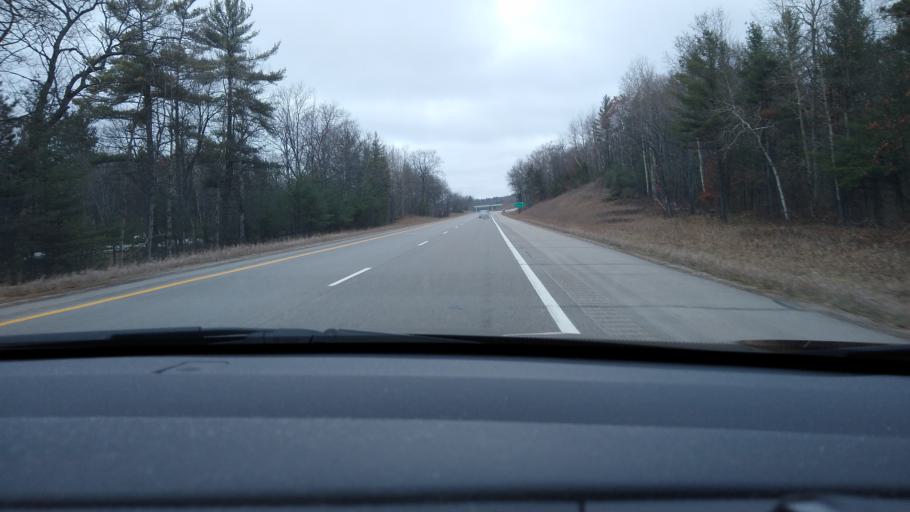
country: US
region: Michigan
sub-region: Otsego County
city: Gaylord
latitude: 44.8687
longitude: -84.6906
